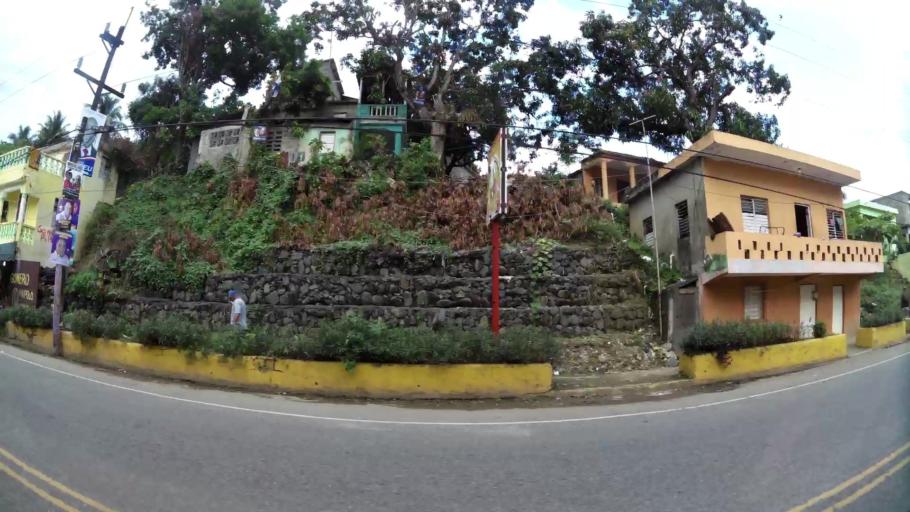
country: DO
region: San Cristobal
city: Villa Altagracia
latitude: 18.6773
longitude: -70.1763
